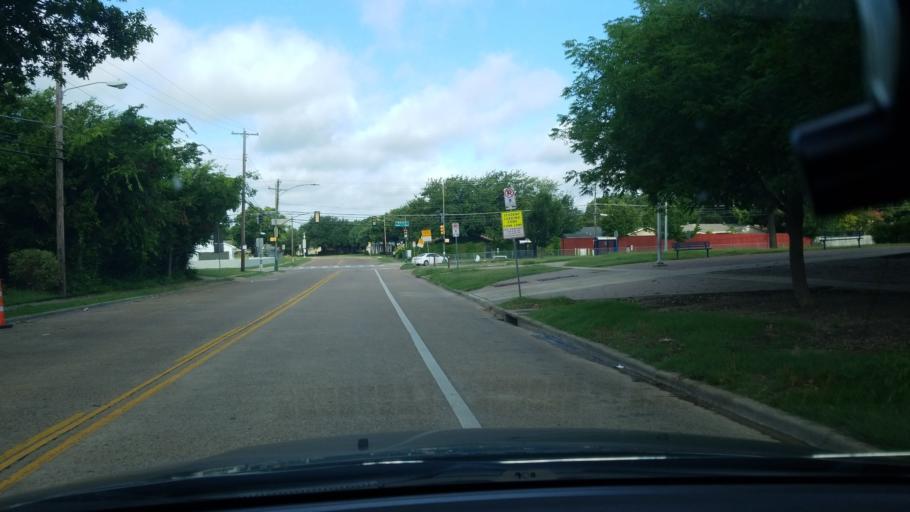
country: US
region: Texas
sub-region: Dallas County
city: Mesquite
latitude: 32.8150
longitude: -96.6835
